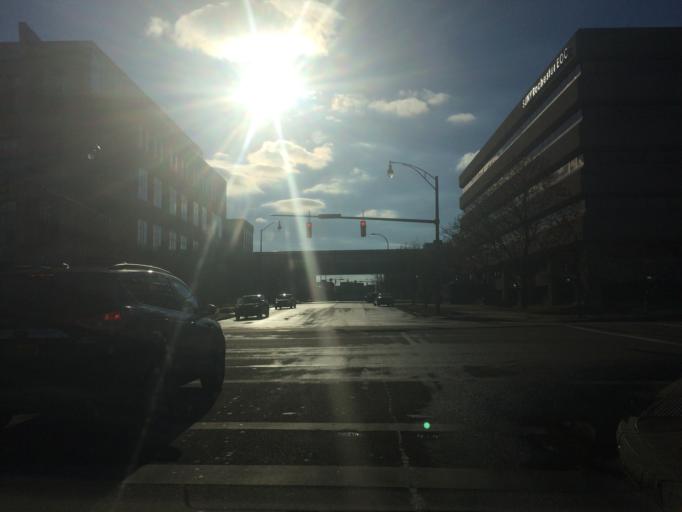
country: US
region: New York
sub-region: Monroe County
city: Rochester
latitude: 43.1532
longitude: -77.6026
